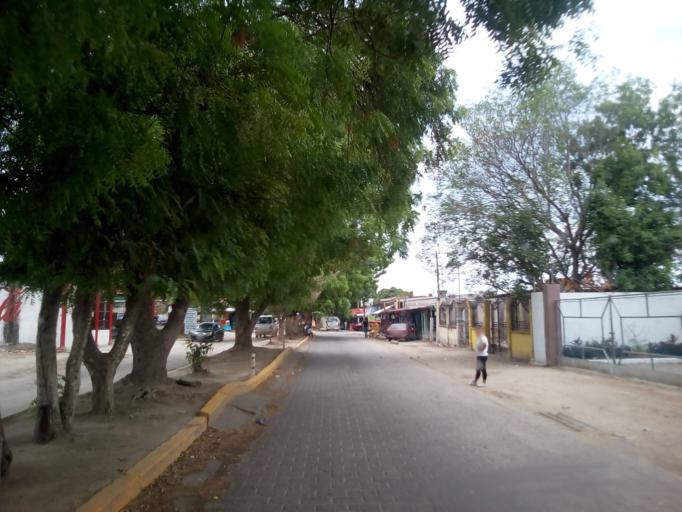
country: HN
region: Cortes
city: La Lima
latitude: 15.4567
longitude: -87.9495
